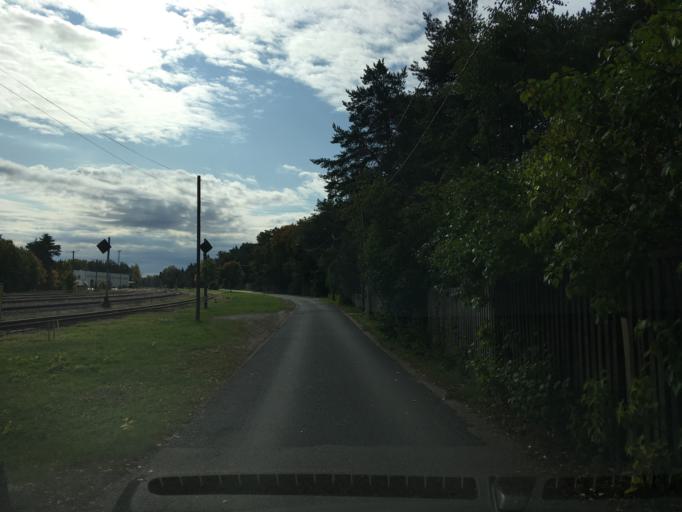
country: EE
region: Harju
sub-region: Tallinna linn
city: Tallinn
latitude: 59.3859
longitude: 24.7214
